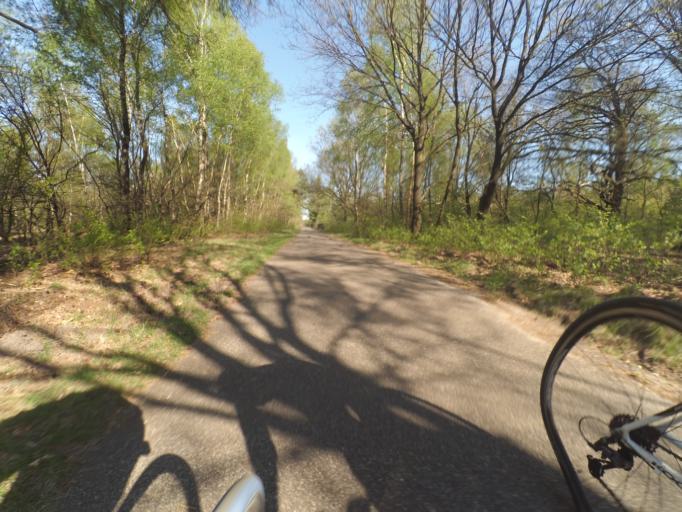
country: NL
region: Gelderland
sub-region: Gemeente Apeldoorn
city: Uddel
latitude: 52.1852
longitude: 5.8117
